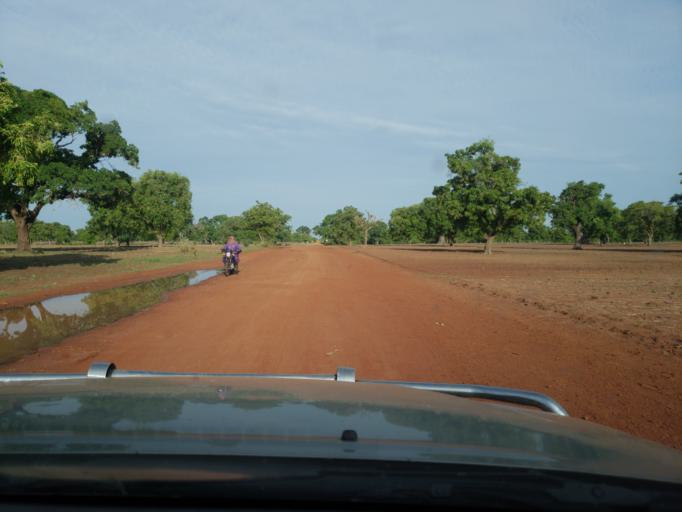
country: ML
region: Sikasso
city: Koutiala
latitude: 12.4193
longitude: -5.7015
